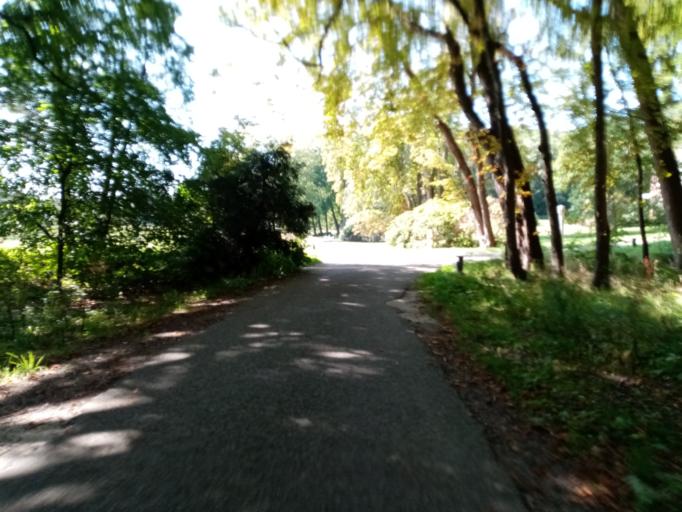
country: NL
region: North Holland
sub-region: Gemeente Bloemendaal
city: Bennebroek
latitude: 52.3410
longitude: 4.5930
